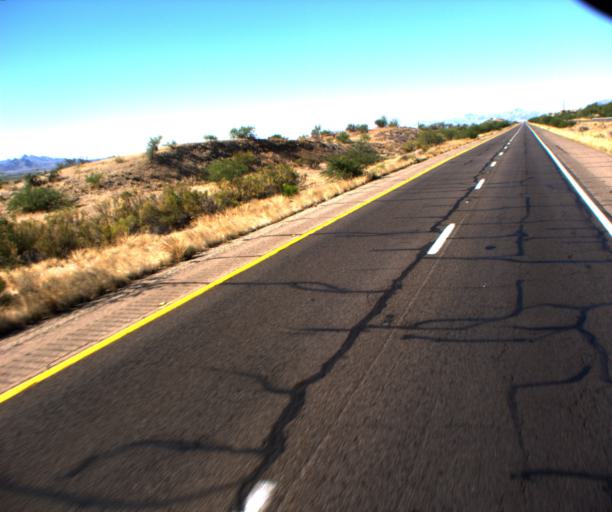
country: US
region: Arizona
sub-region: Pima County
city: Green Valley
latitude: 31.8190
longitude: -111.0066
